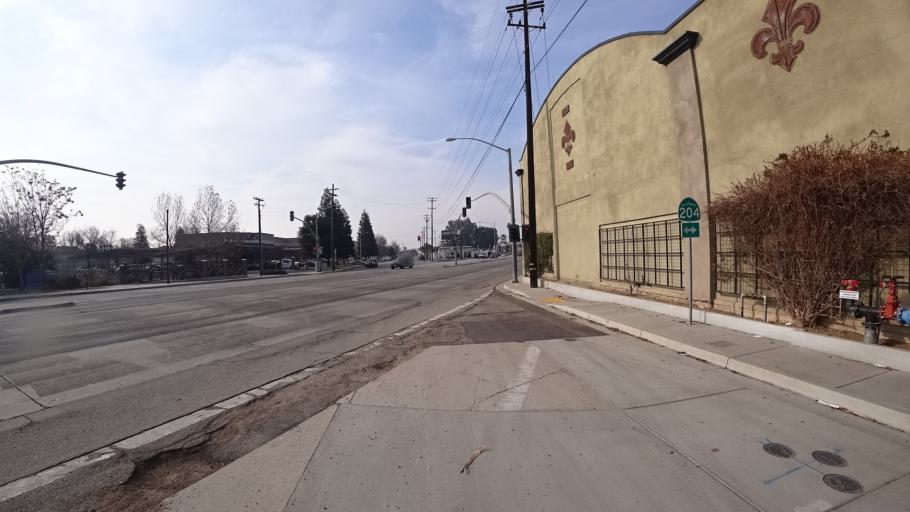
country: US
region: California
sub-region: Kern County
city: Bakersfield
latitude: 35.3810
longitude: -119.0065
